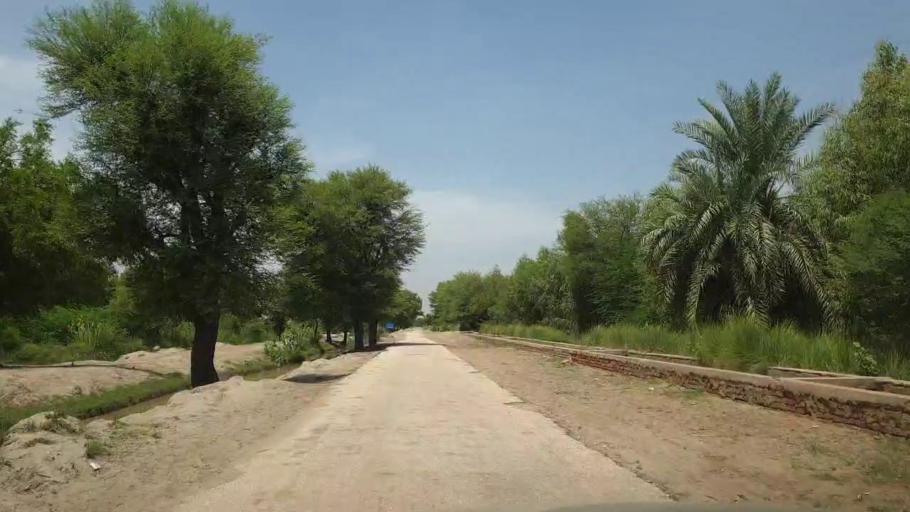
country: PK
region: Sindh
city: Kot Diji
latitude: 27.1350
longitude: 69.0261
